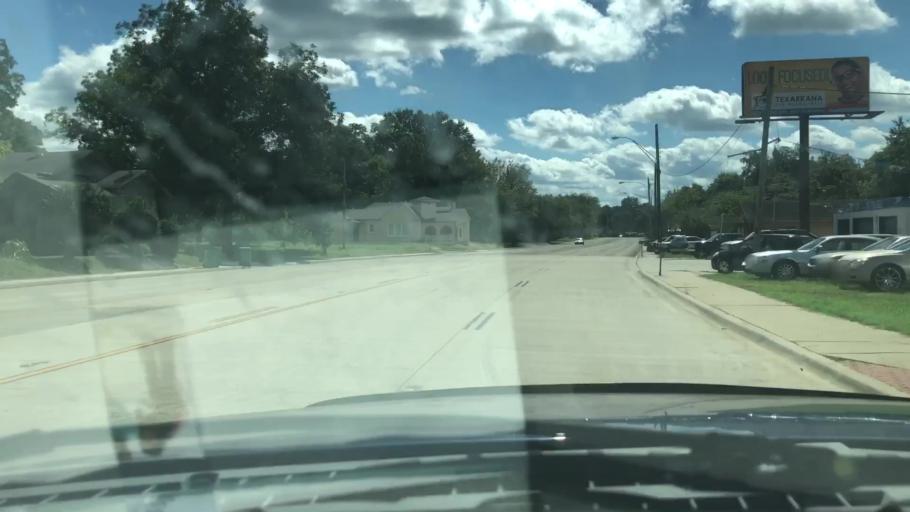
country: US
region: Texas
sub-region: Bowie County
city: Texarkana
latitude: 33.4108
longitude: -94.0607
